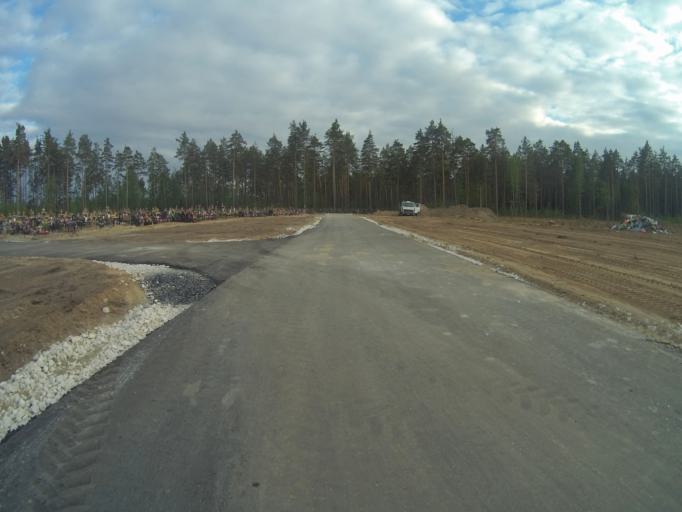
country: RU
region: Vladimir
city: Golovino
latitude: 56.0301
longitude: 40.4177
